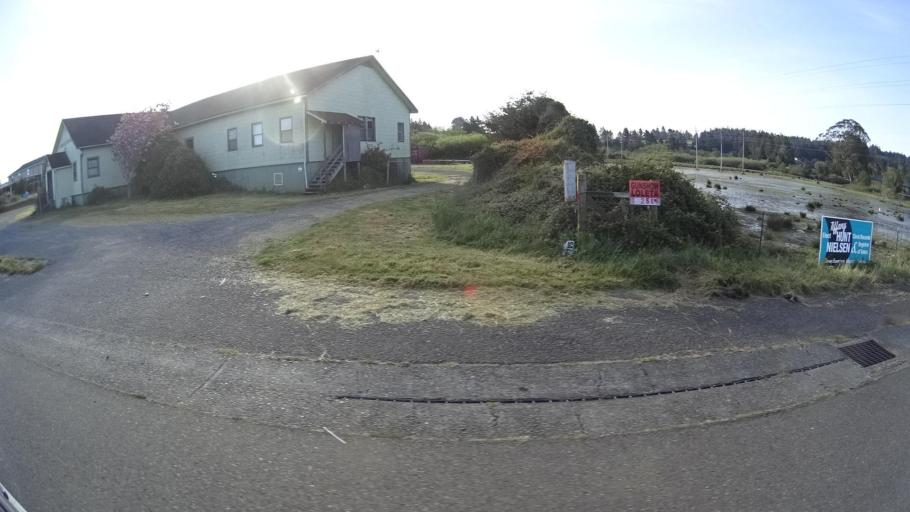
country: US
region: California
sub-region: Humboldt County
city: Humboldt Hill
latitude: 40.7387
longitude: -124.1999
